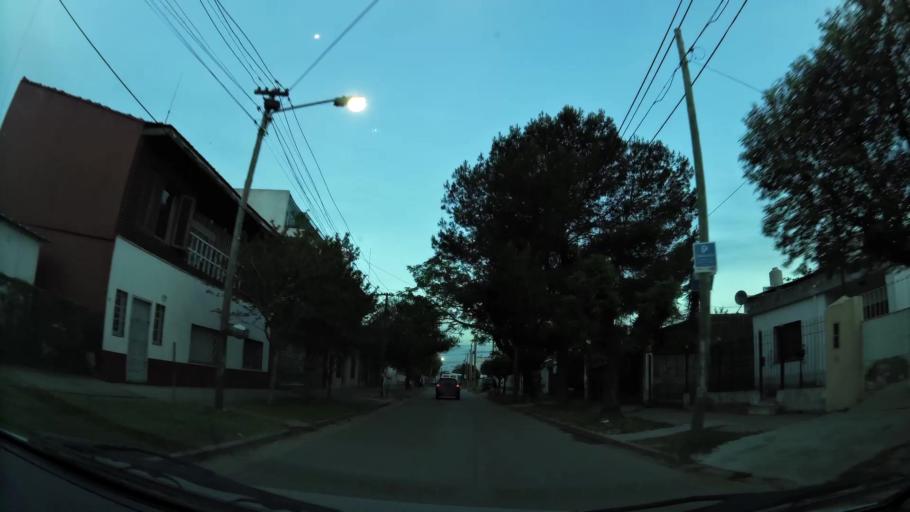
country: AR
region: Buenos Aires
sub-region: Partido de Quilmes
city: Quilmes
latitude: -34.7976
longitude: -58.2815
